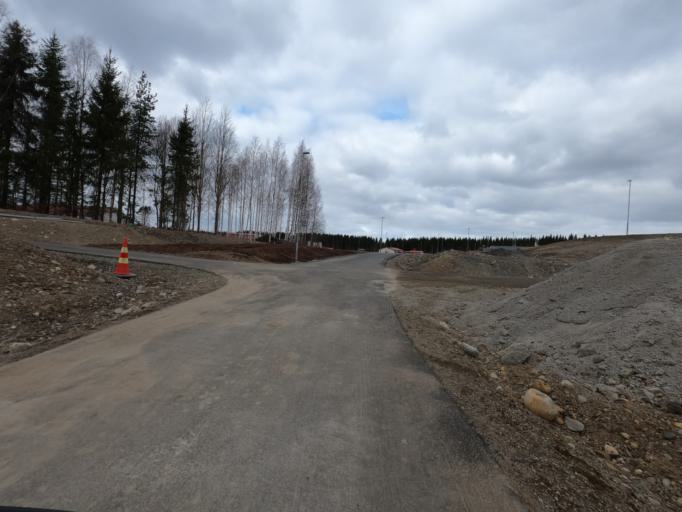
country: FI
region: North Karelia
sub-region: Joensuu
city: Joensuu
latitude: 62.5571
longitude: 29.8265
